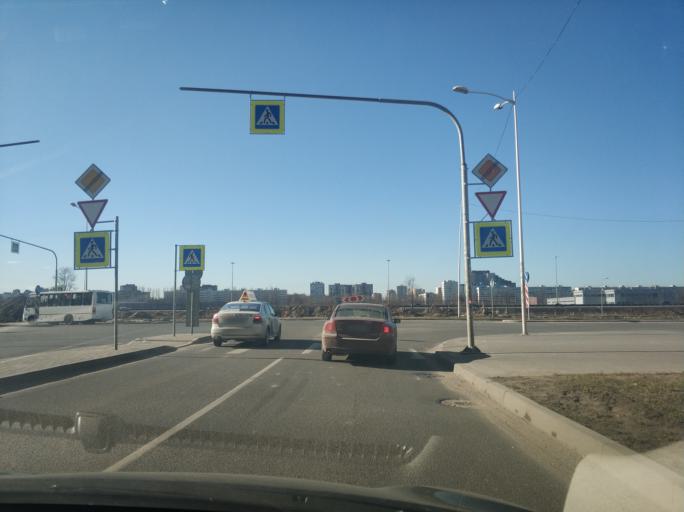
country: RU
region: St.-Petersburg
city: Grazhdanka
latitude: 60.0502
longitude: 30.4229
